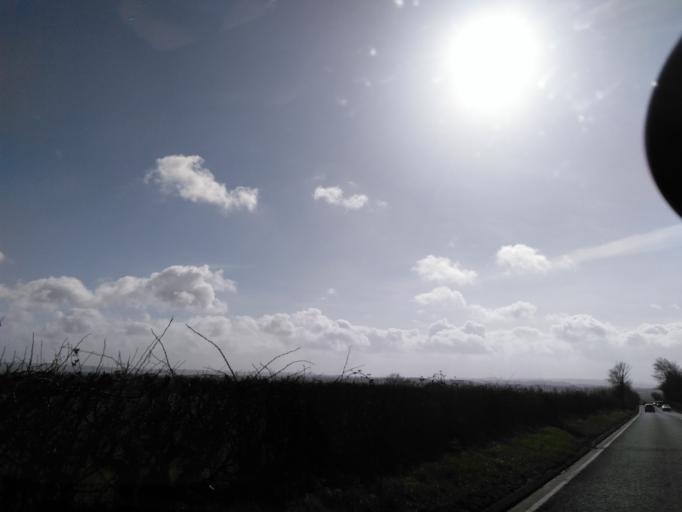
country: GB
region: England
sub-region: Bath and North East Somerset
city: Hinton Charterhouse
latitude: 51.2971
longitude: -2.3039
